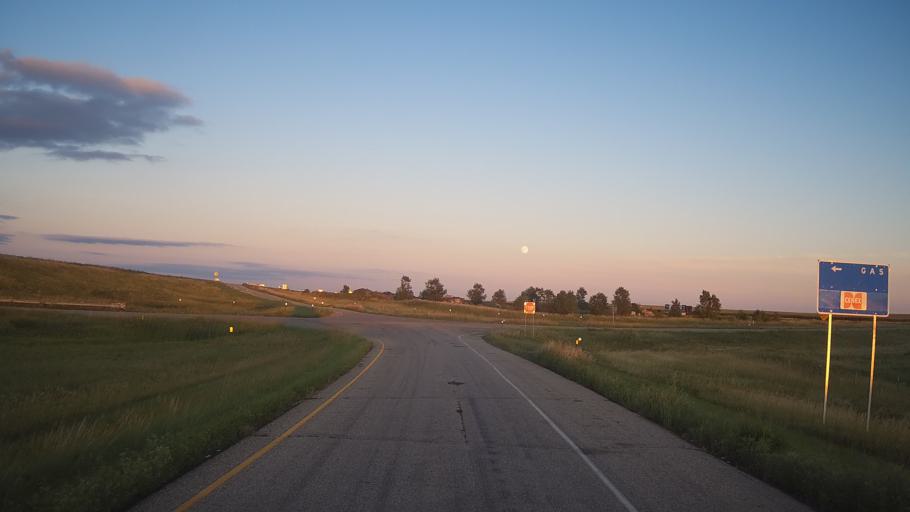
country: US
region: South Dakota
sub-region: Lyman County
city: Kennebec
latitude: 43.8639
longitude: -99.6069
